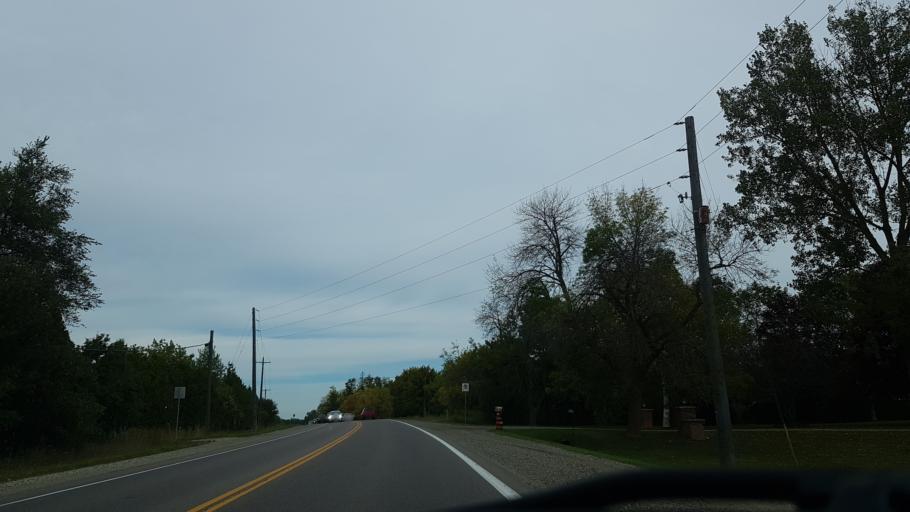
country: CA
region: Ontario
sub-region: Wellington County
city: Guelph
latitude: 43.5961
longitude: -80.2360
